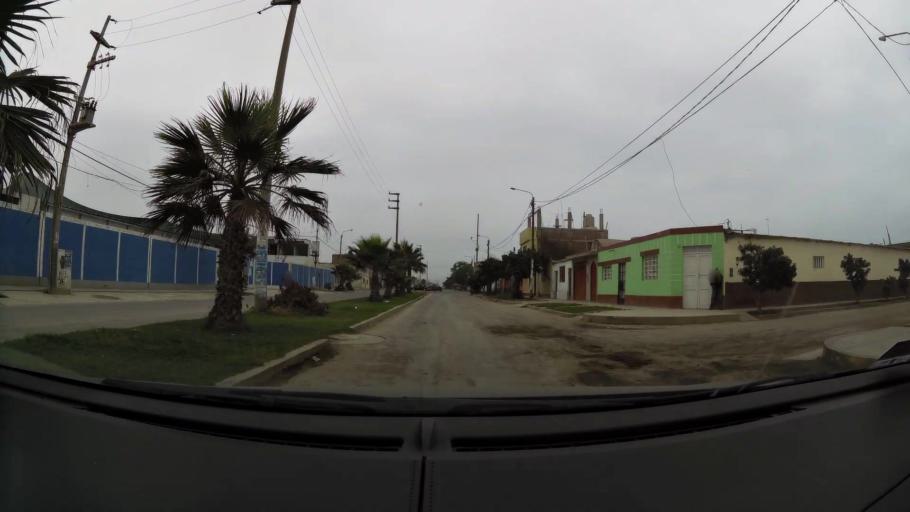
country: PE
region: La Libertad
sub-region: Provincia de Trujillo
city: Buenos Aires
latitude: -8.1449
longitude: -79.0513
